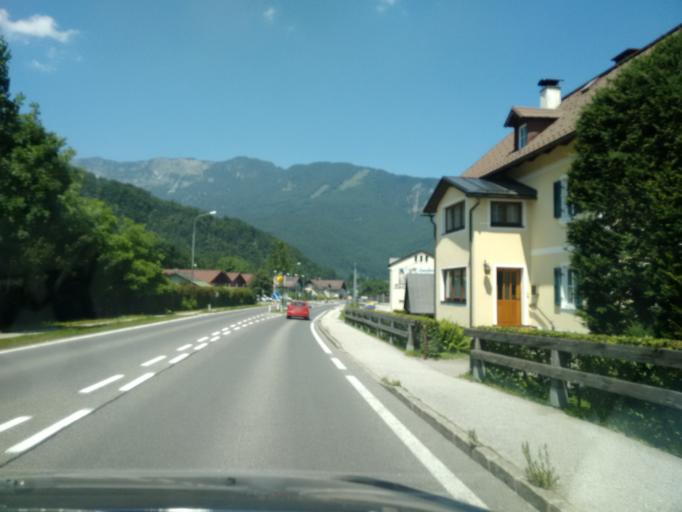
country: AT
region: Upper Austria
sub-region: Politischer Bezirk Gmunden
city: Bad Goisern
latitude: 47.6537
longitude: 13.6106
